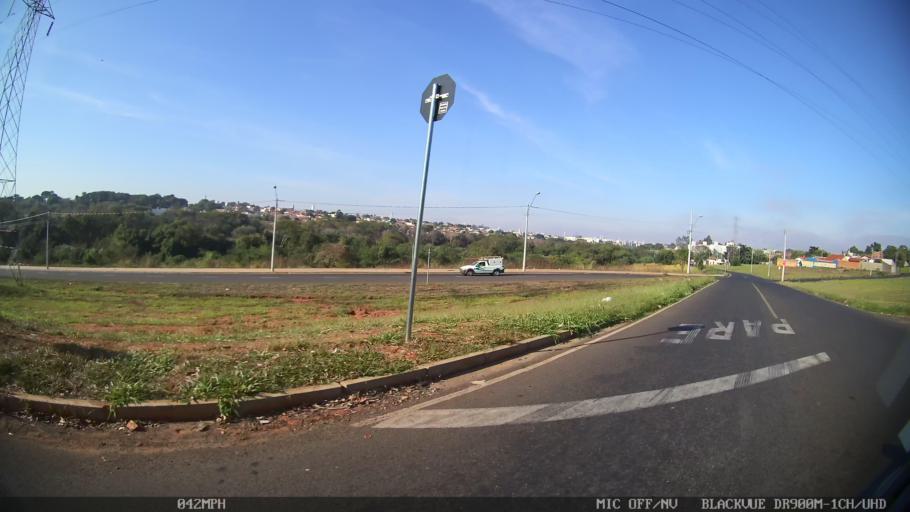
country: BR
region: Sao Paulo
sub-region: Sao Jose Do Rio Preto
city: Sao Jose do Rio Preto
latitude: -20.7639
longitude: -49.3785
